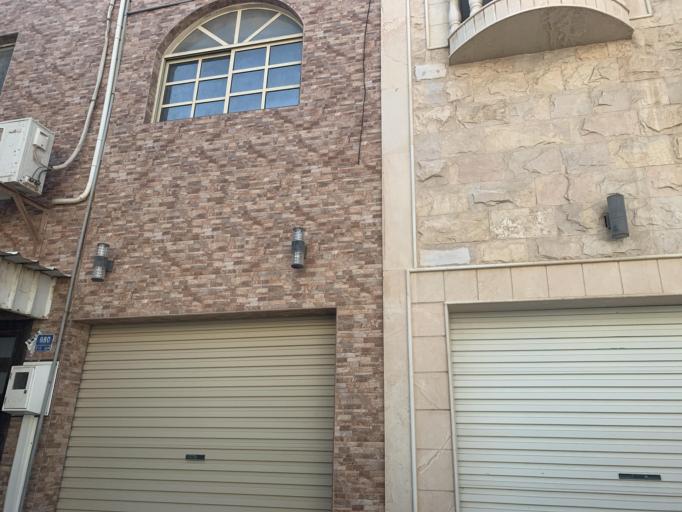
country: BH
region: Central Governorate
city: Madinat Hamad
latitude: 26.1369
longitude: 50.4974
